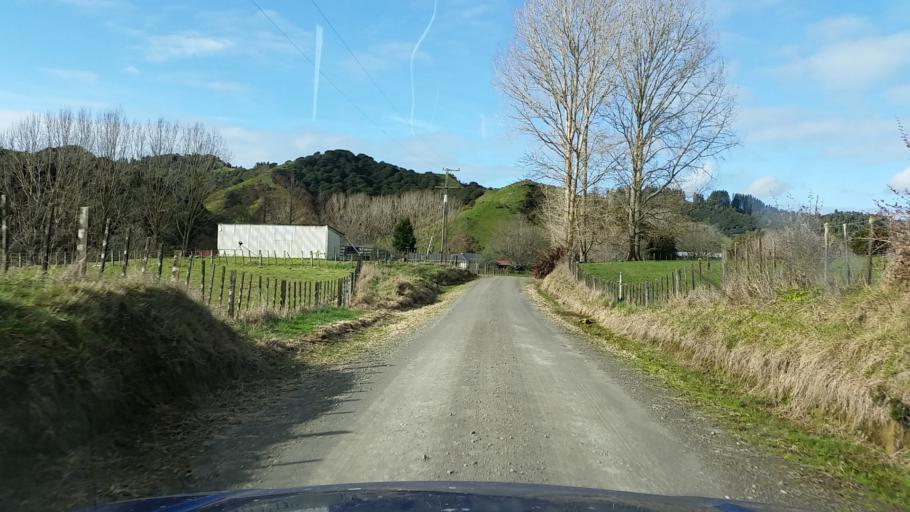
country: NZ
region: Taranaki
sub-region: South Taranaki District
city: Eltham
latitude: -39.2596
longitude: 174.5891
